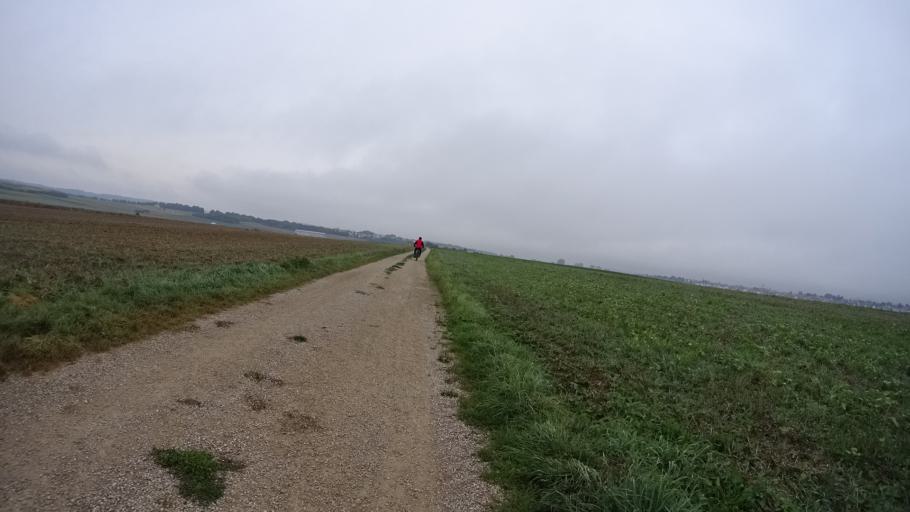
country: DE
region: Bavaria
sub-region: Upper Bavaria
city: Wettstetten
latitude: 48.8163
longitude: 11.3908
